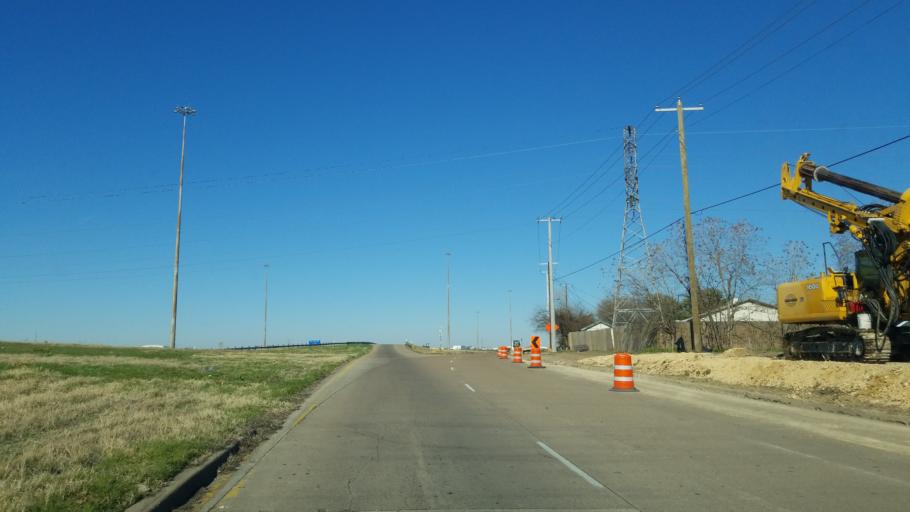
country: US
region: Texas
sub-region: Tarrant County
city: Arlington
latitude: 32.7138
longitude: -97.0613
